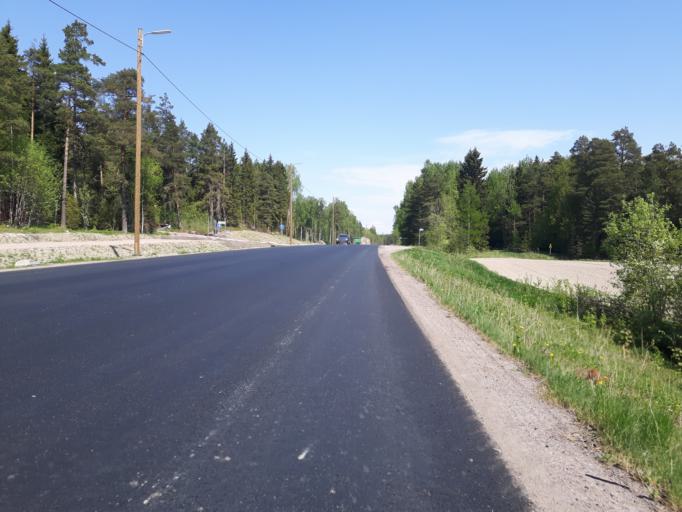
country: FI
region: Uusimaa
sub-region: Porvoo
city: Porvoo
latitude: 60.3604
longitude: 25.5379
